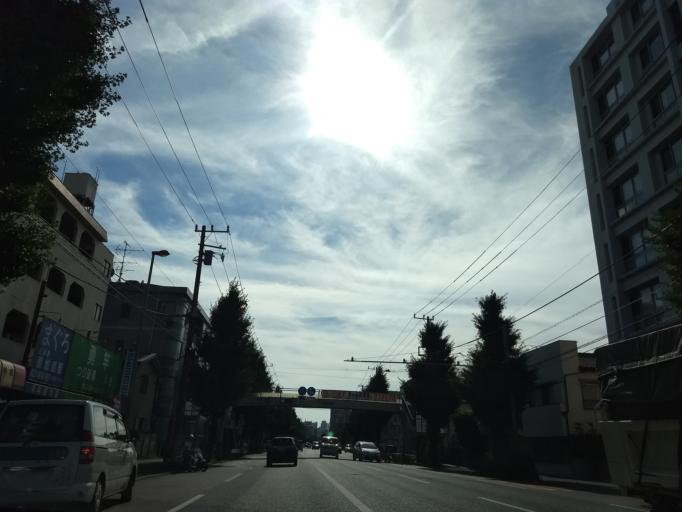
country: JP
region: Kanagawa
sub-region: Kawasaki-shi
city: Kawasaki
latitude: 35.5295
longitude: 139.7271
